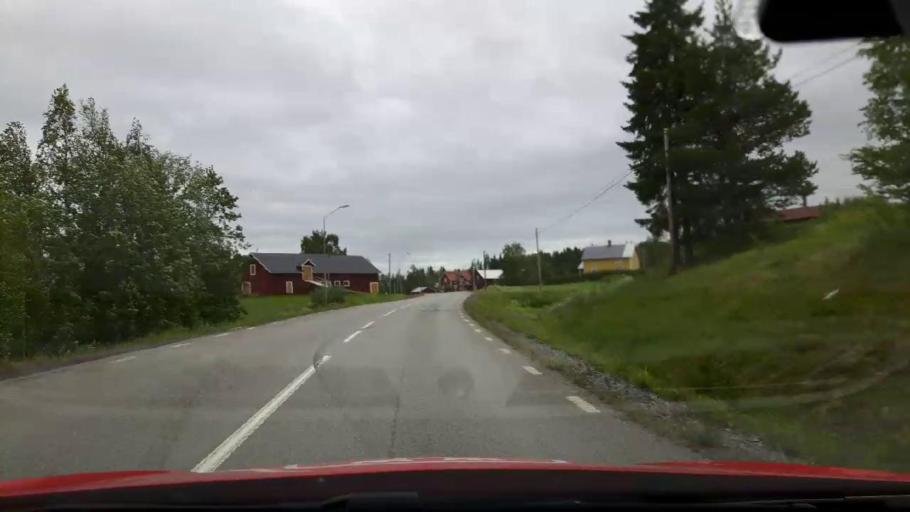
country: SE
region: Jaemtland
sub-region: OEstersunds Kommun
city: Lit
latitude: 63.6796
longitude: 15.0443
